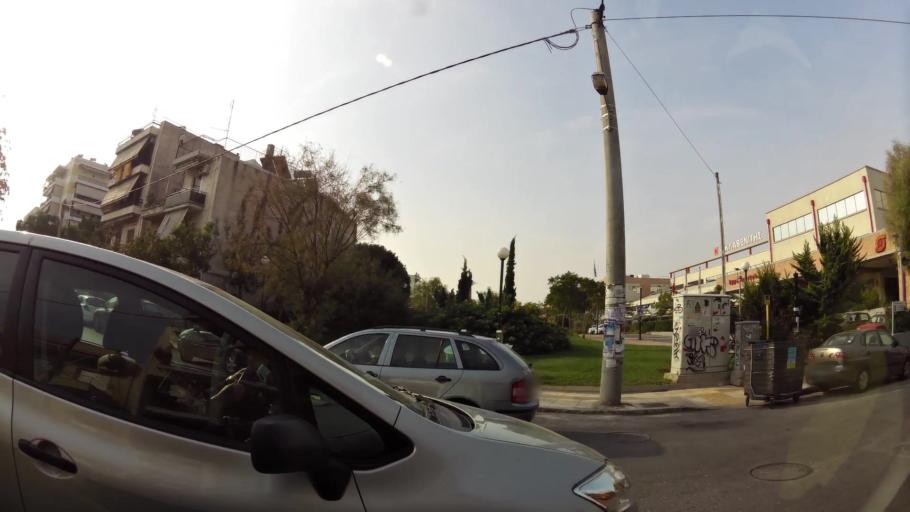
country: GR
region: Attica
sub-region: Nomarchia Athinas
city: Moskhaton
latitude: 37.9482
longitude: 23.6869
